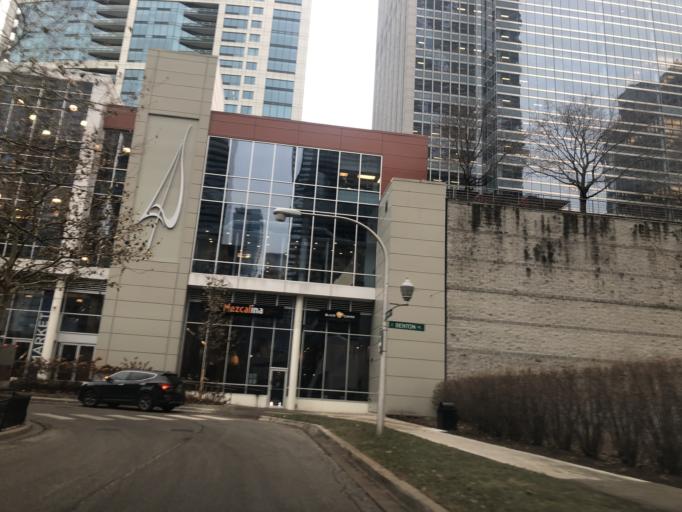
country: US
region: Illinois
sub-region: Cook County
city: Chicago
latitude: 41.8857
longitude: -87.6191
